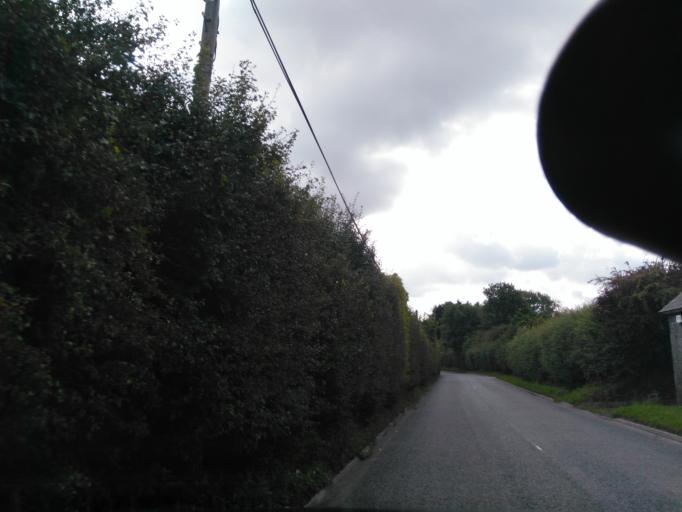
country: GB
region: England
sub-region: Dorset
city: Shaftesbury
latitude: 50.9992
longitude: -2.1796
